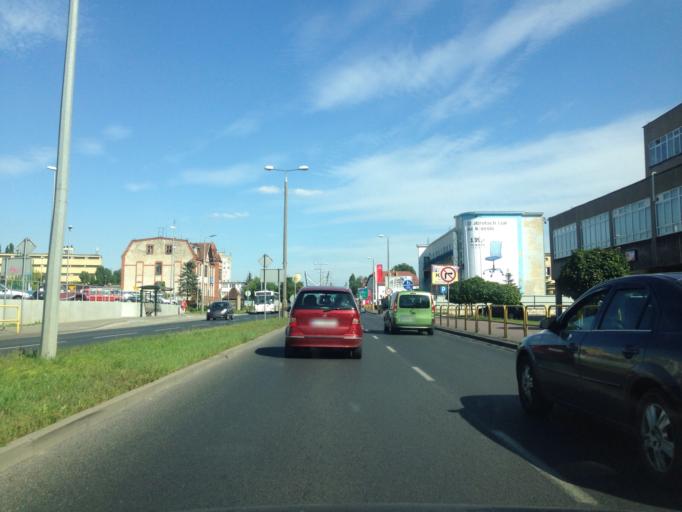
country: PL
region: Kujawsko-Pomorskie
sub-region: Torun
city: Torun
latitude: 53.0233
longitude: 18.6392
